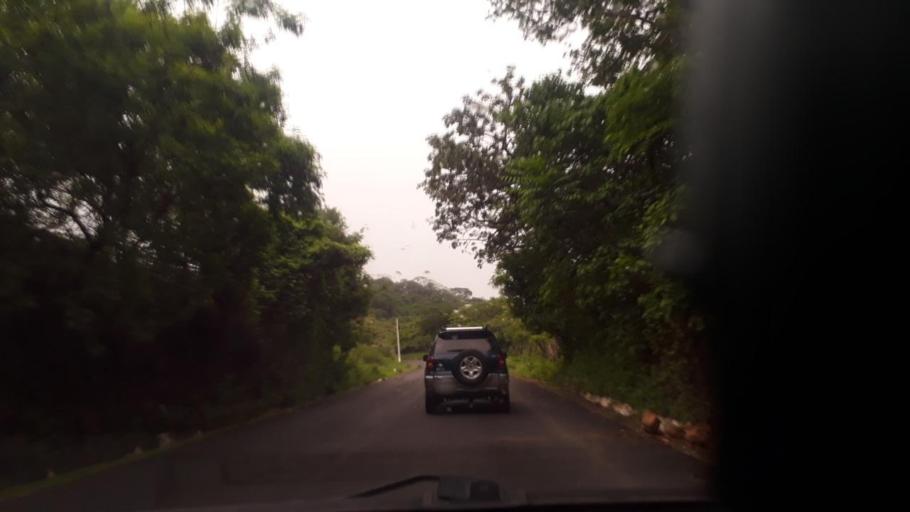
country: GT
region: Jutiapa
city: Jalpatagua
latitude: 14.1671
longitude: -90.0466
